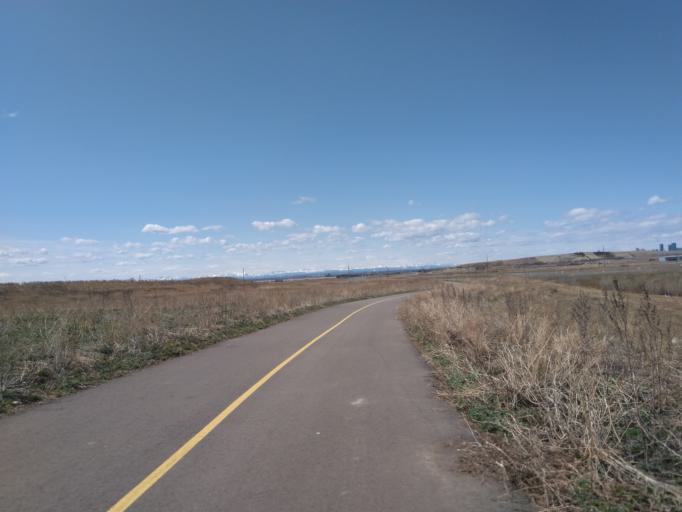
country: CA
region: Alberta
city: Chestermere
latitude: 51.0169
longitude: -113.9284
